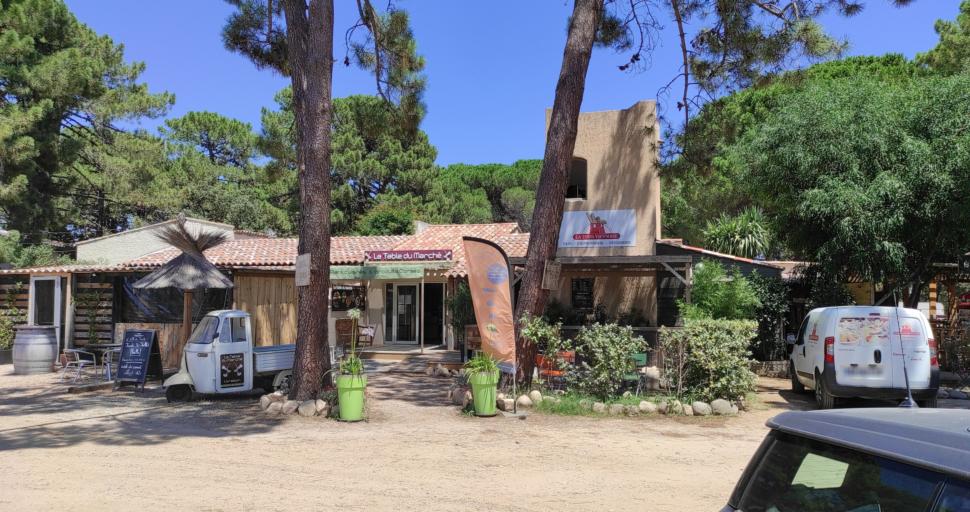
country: FR
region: Corsica
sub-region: Departement de la Corse-du-Sud
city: Porto-Vecchio
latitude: 41.6297
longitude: 9.3340
